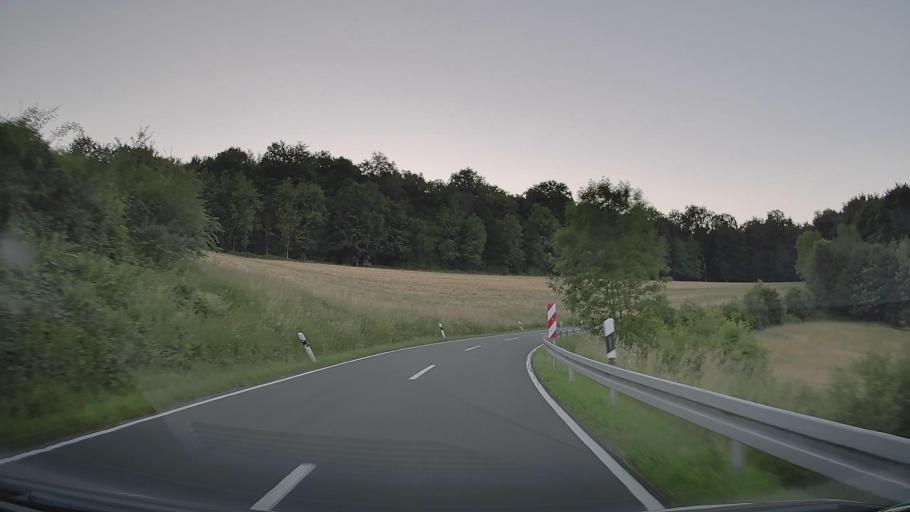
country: DE
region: Lower Saxony
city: Bad Pyrmont
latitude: 51.9975
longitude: 9.2107
